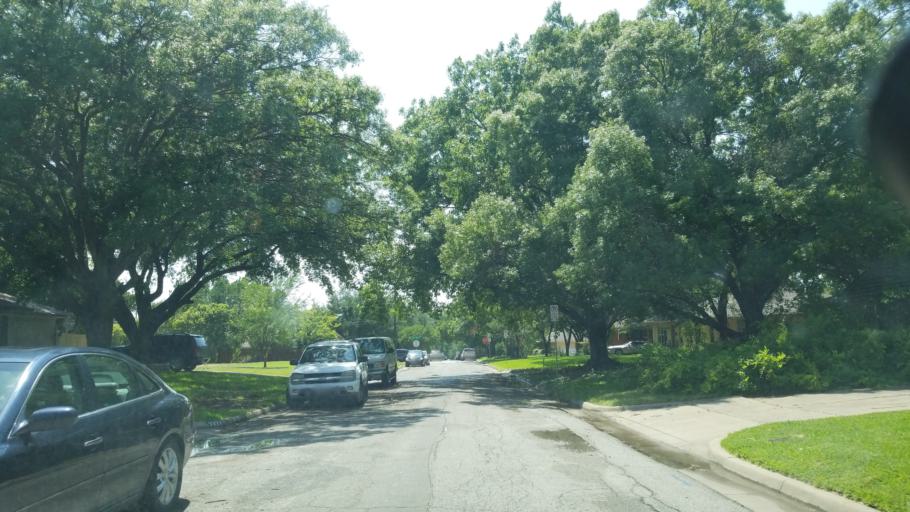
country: US
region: Texas
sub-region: Dallas County
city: Farmers Branch
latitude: 32.8790
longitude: -96.8705
